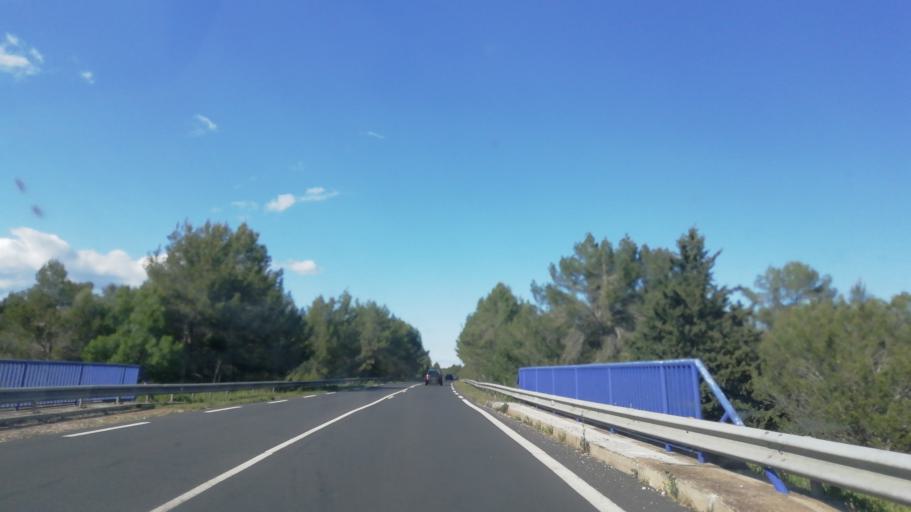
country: FR
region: Languedoc-Roussillon
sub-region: Departement de l'Herault
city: Saint-Clement-de-Riviere
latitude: 43.6883
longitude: 3.8233
